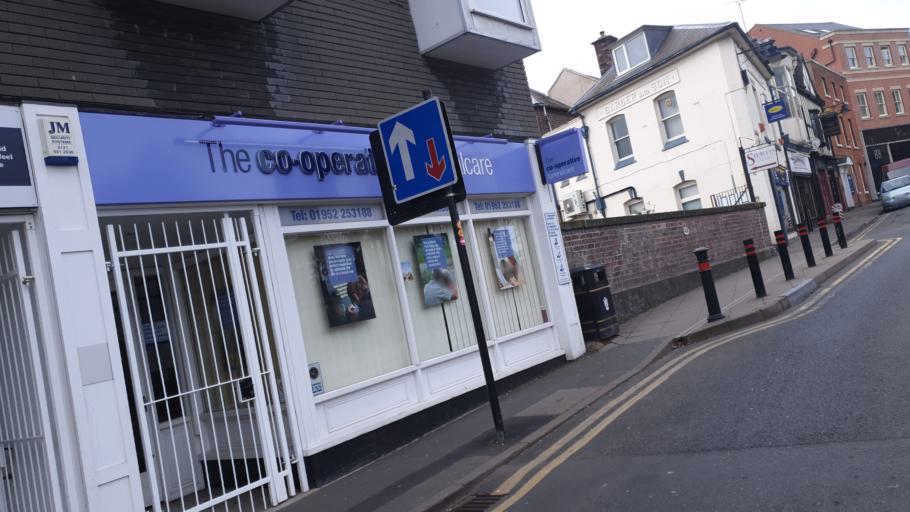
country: GB
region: England
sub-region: Telford and Wrekin
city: Wellington
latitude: 52.7014
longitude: -2.5187
